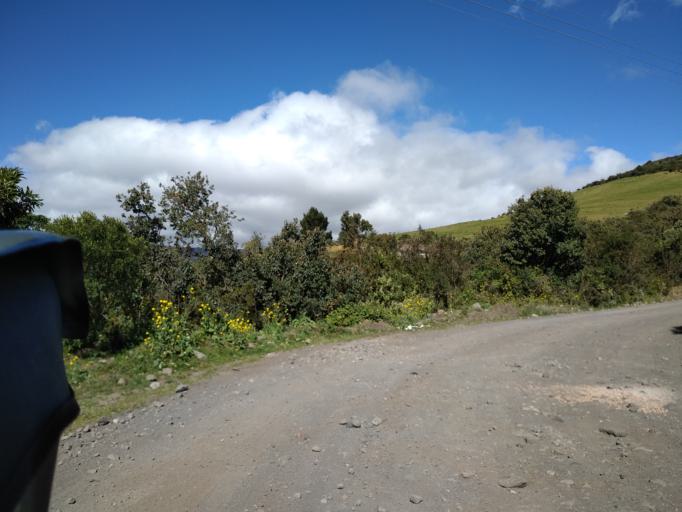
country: EC
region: Pichincha
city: Machachi
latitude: -0.5328
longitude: -78.4822
